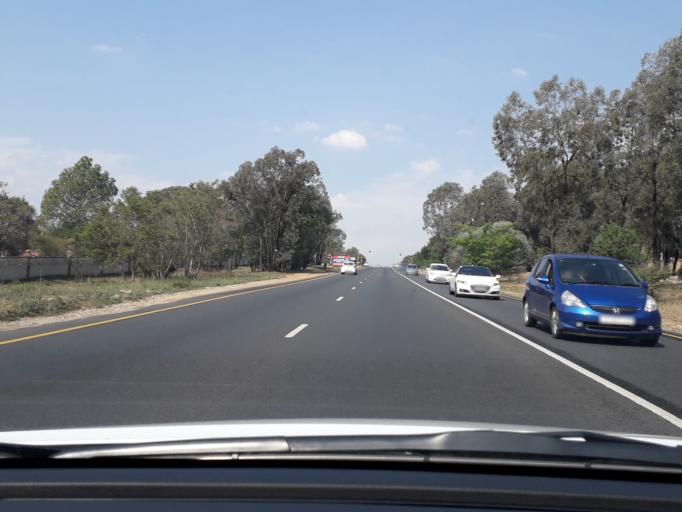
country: ZA
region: Gauteng
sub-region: City of Johannesburg Metropolitan Municipality
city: Diepsloot
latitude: -26.0279
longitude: 27.9809
